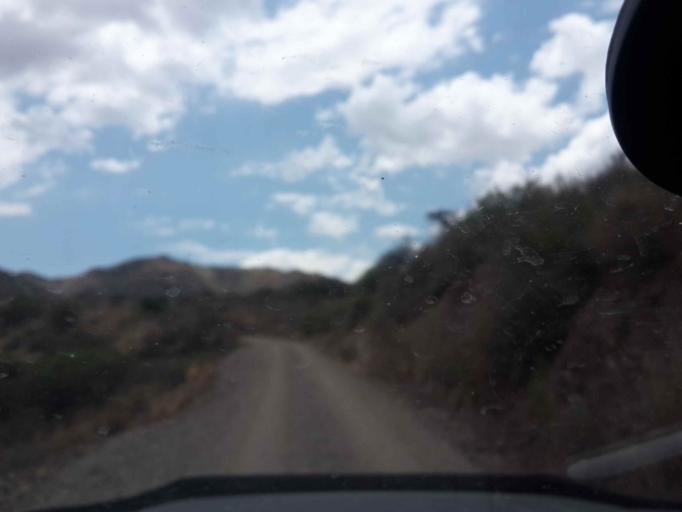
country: BO
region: Cochabamba
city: Sipe Sipe
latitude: -17.5322
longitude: -66.4936
